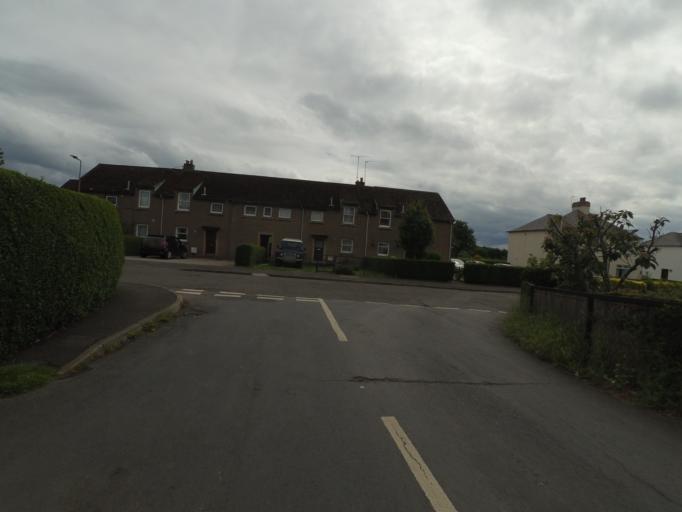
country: GB
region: Scotland
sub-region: East Lothian
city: Ormiston
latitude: 55.9127
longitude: -2.9359
